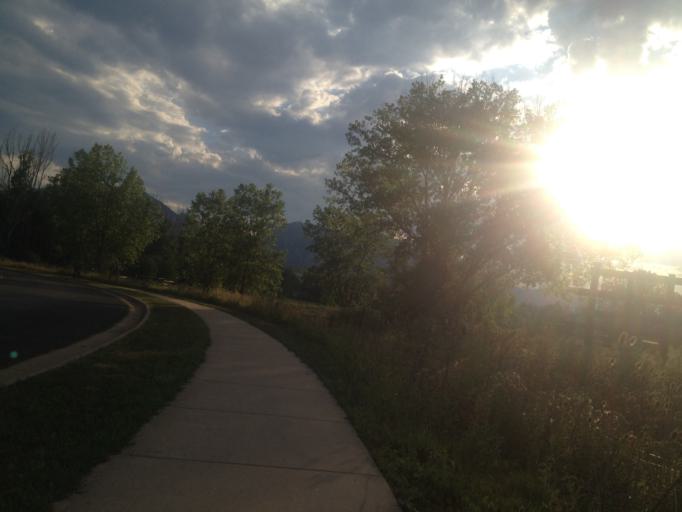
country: US
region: Colorado
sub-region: Boulder County
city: Boulder
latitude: 39.9902
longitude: -105.2228
